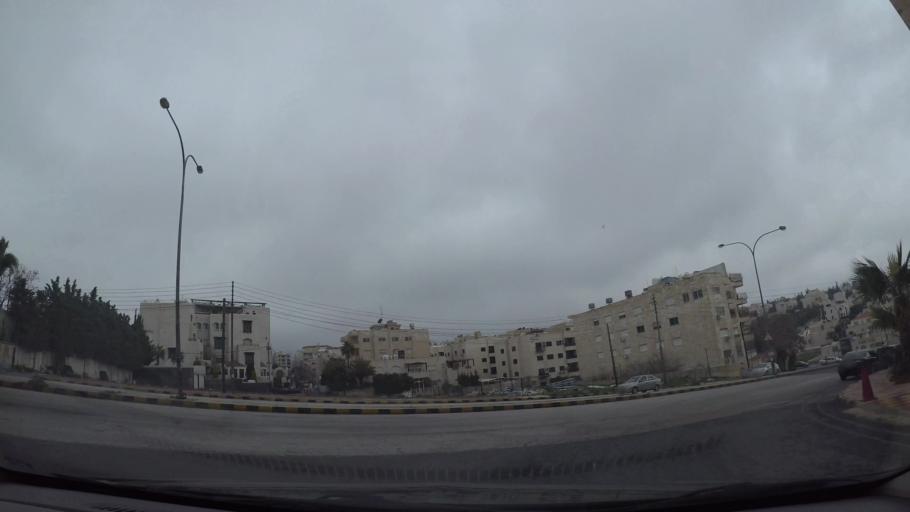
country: JO
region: Amman
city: Wadi as Sir
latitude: 31.9427
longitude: 35.8689
